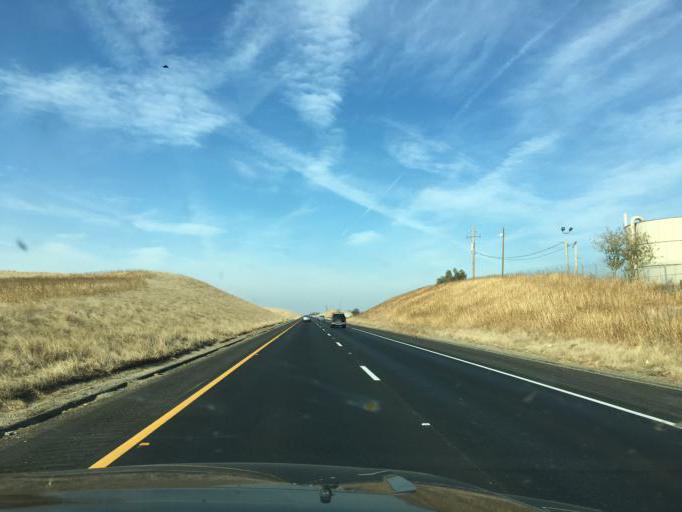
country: US
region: California
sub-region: Fresno County
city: Coalinga
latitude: 36.3057
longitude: -120.2775
